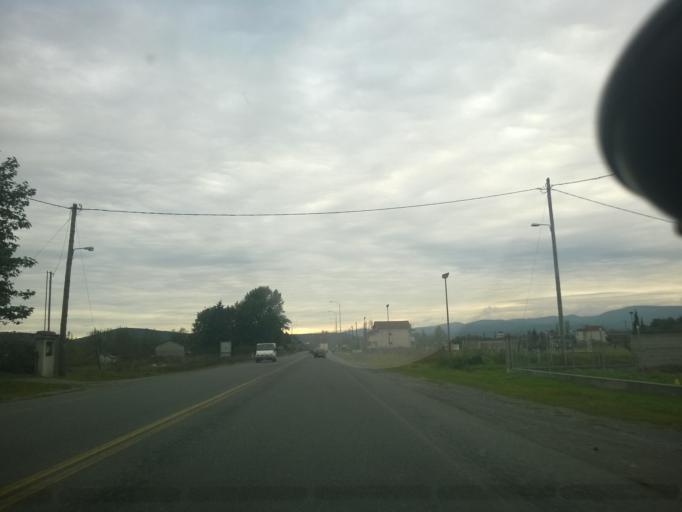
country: GR
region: Central Macedonia
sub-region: Nomos Pellis
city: Aridaia
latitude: 40.9378
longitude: 22.0840
